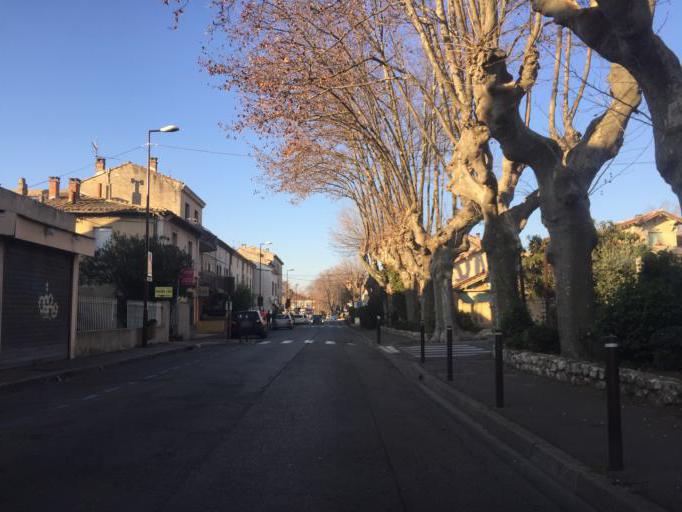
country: FR
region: Provence-Alpes-Cote d'Azur
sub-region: Departement du Vaucluse
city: Montfavet
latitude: 43.9343
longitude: 4.8723
